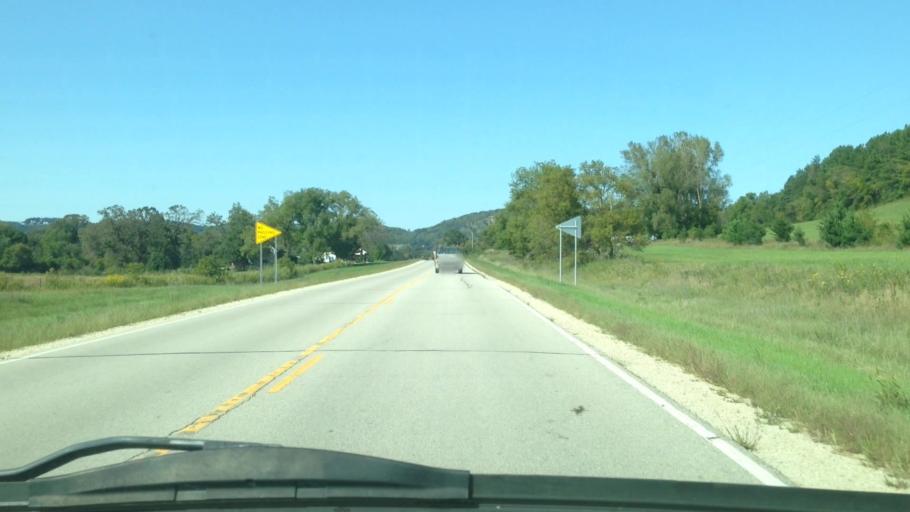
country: US
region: Minnesota
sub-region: Fillmore County
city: Rushford
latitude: 43.7819
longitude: -91.7648
